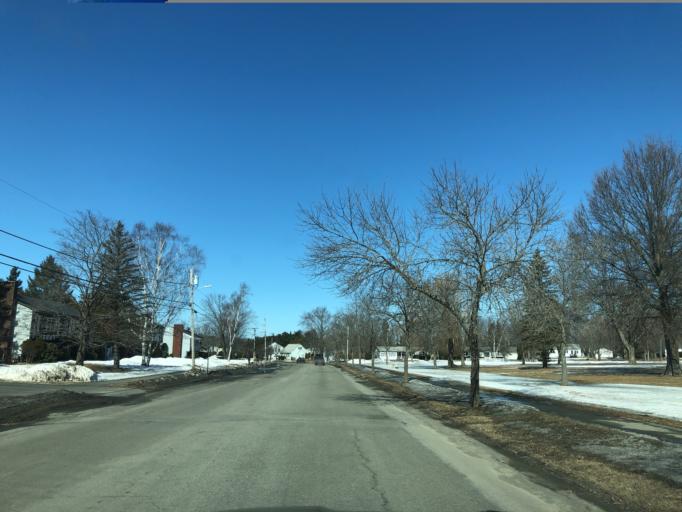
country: US
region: Maine
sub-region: Penobscot County
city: Brewer
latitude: 44.8189
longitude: -68.7580
